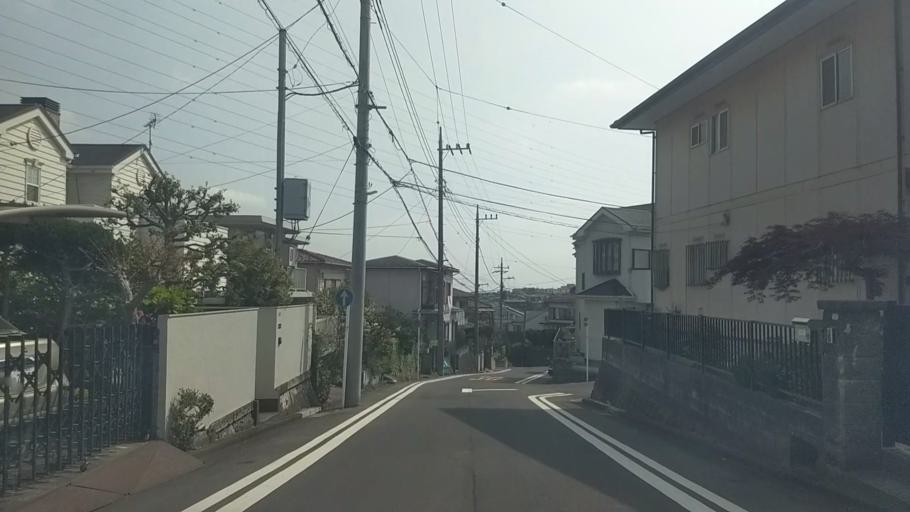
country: JP
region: Kanagawa
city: Yokohama
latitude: 35.3747
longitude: 139.6150
